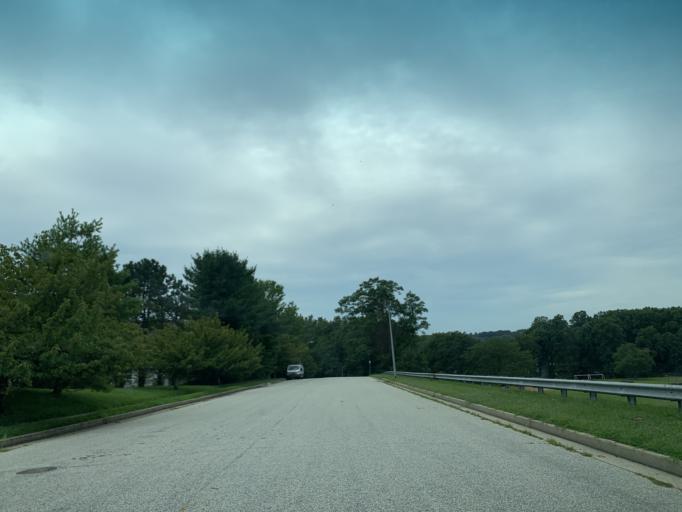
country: US
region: Maryland
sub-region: Baltimore County
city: Carney
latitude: 39.4100
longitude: -76.5273
